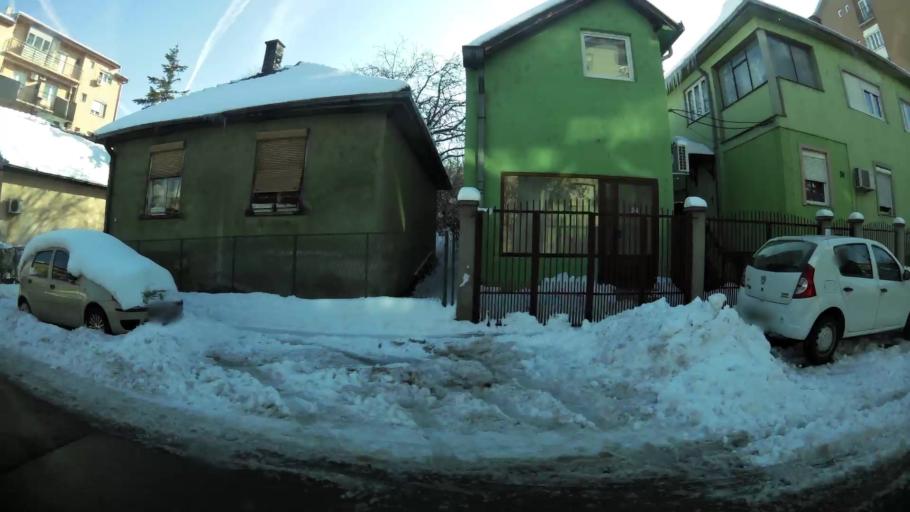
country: RS
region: Central Serbia
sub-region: Belgrade
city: Palilula
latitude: 44.8132
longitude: 20.5081
